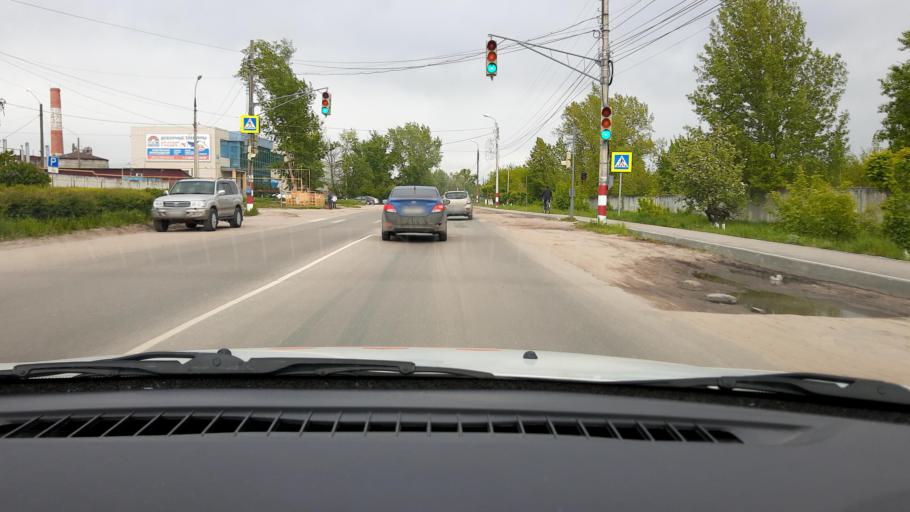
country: RU
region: Nizjnij Novgorod
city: Bor
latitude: 56.3508
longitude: 44.0780
